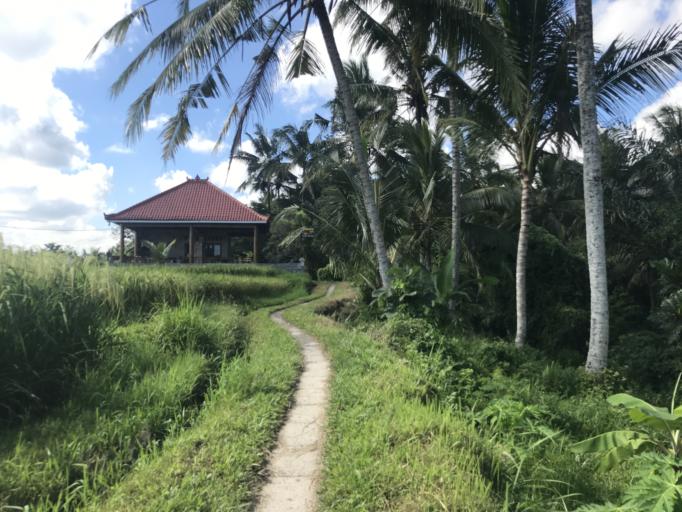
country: ID
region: Bali
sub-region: Kabupaten Gianyar
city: Ubud
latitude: -8.4916
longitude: 115.2617
